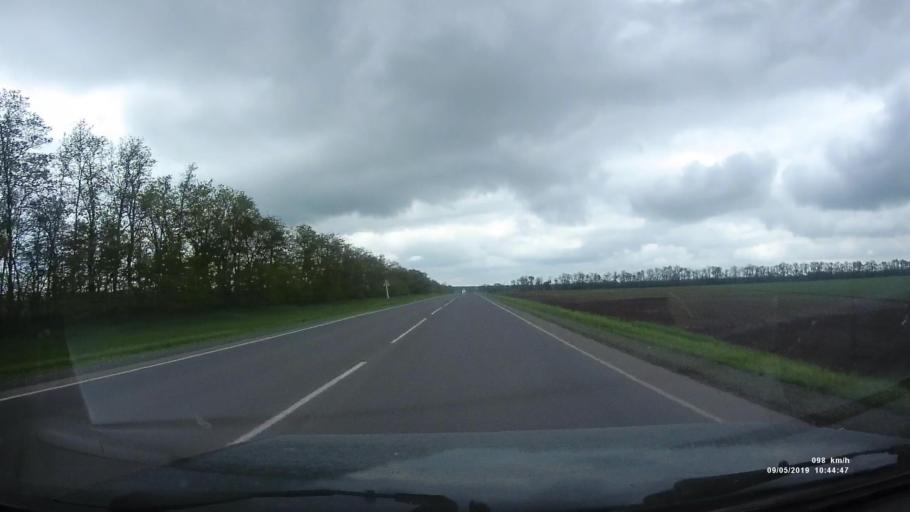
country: RU
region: Rostov
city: Peshkovo
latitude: 46.9996
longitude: 39.3804
